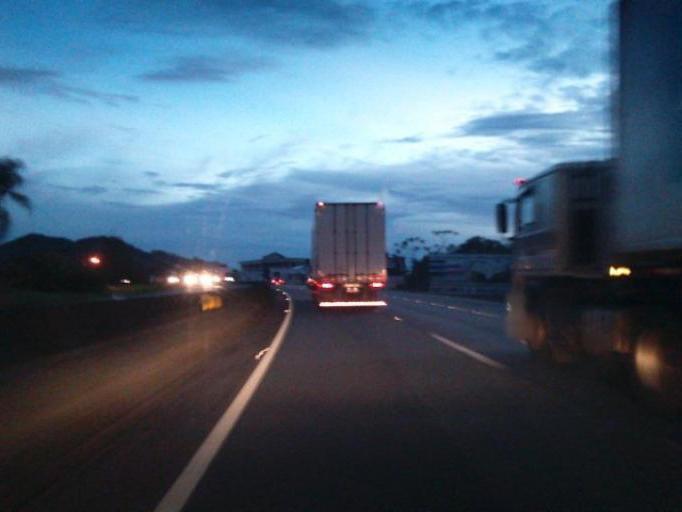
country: BR
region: Santa Catarina
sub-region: Barra Velha
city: Barra Velha
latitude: -26.5570
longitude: -48.7208
